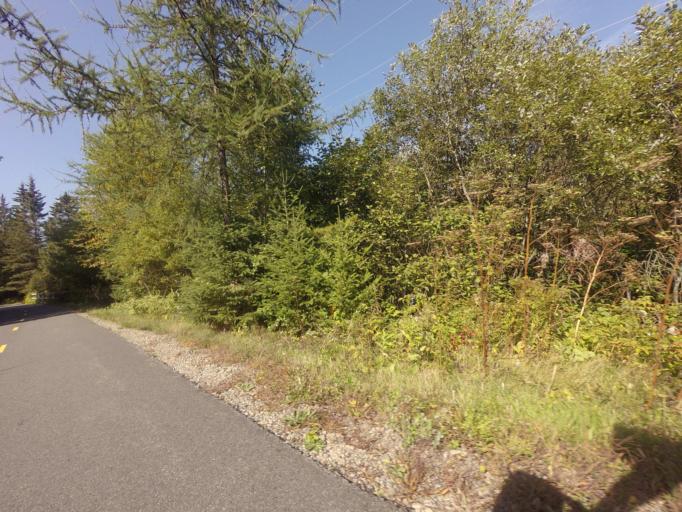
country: CA
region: Quebec
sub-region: Laurentides
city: Mont-Tremblant
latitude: 46.1291
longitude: -74.5509
